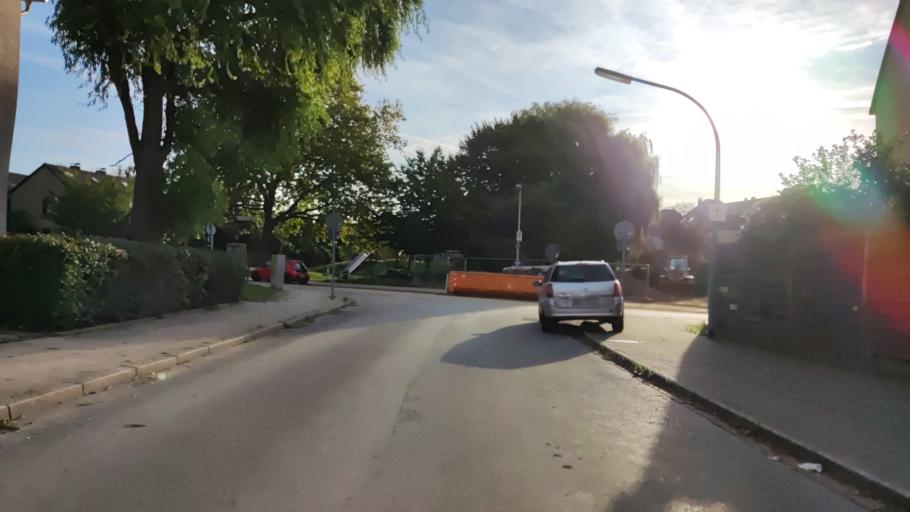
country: DE
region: North Rhine-Westphalia
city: Castrop-Rauxel
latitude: 51.5506
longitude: 7.2805
